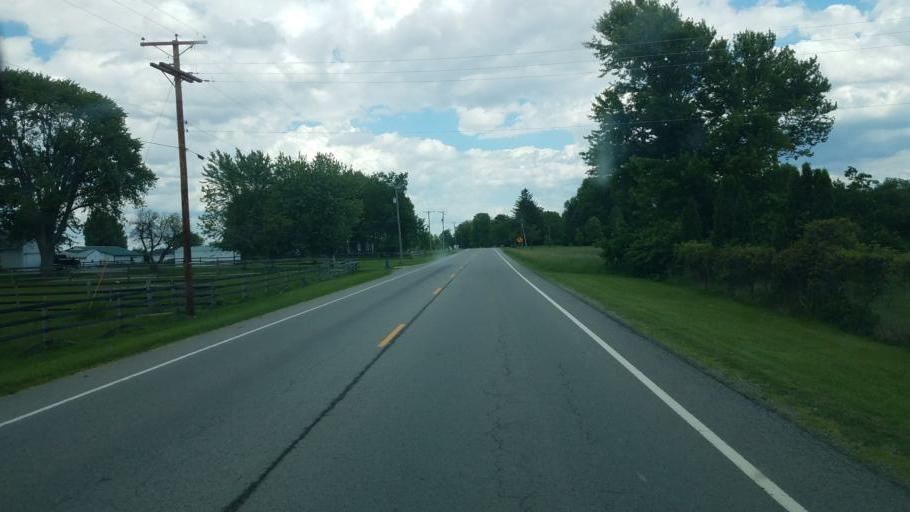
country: US
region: Ohio
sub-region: Crawford County
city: Galion
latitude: 40.8131
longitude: -82.8523
